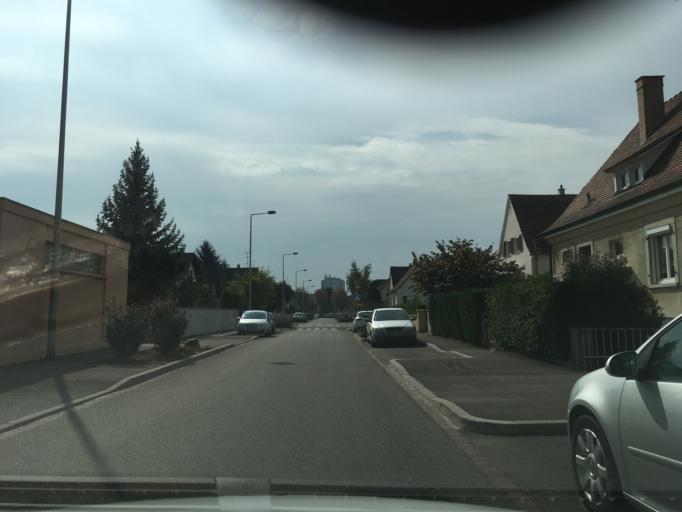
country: FR
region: Alsace
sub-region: Departement du Haut-Rhin
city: Colmar
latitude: 48.0898
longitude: 7.3677
